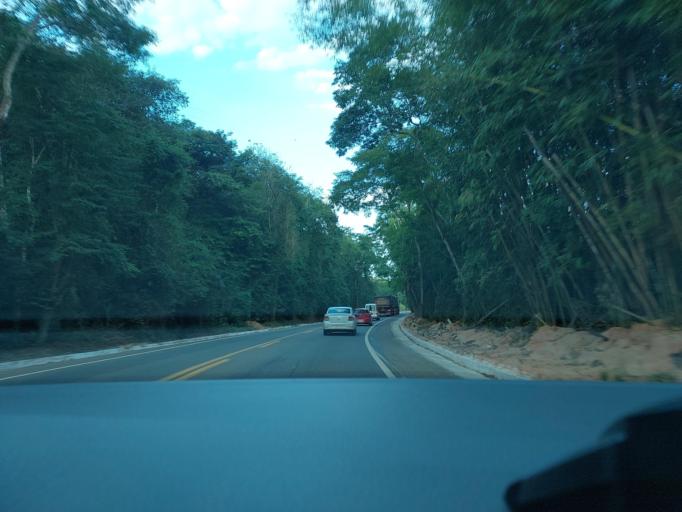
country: BR
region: Minas Gerais
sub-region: Muriae
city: Muriae
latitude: -21.1219
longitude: -42.2222
